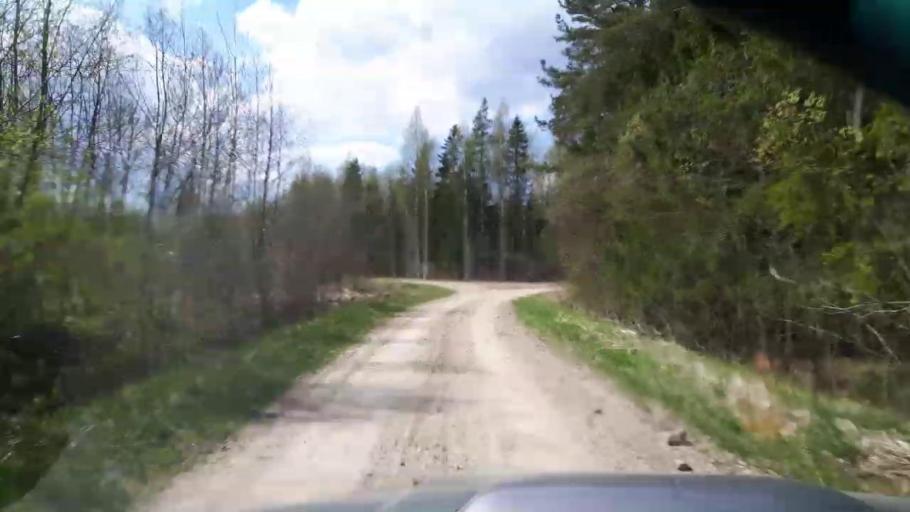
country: EE
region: Paernumaa
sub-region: Tootsi vald
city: Tootsi
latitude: 58.4431
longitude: 24.9221
